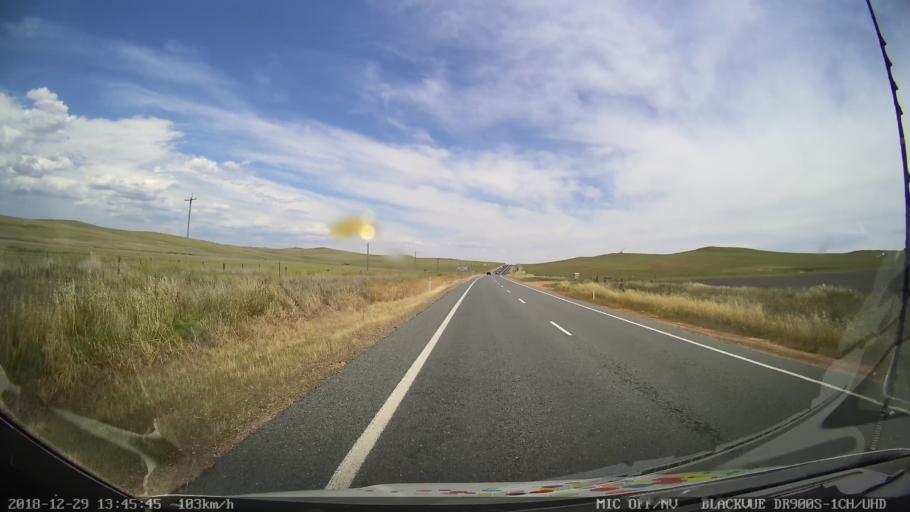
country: AU
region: New South Wales
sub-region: Cooma-Monaro
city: Cooma
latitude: -36.1014
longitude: 149.1451
